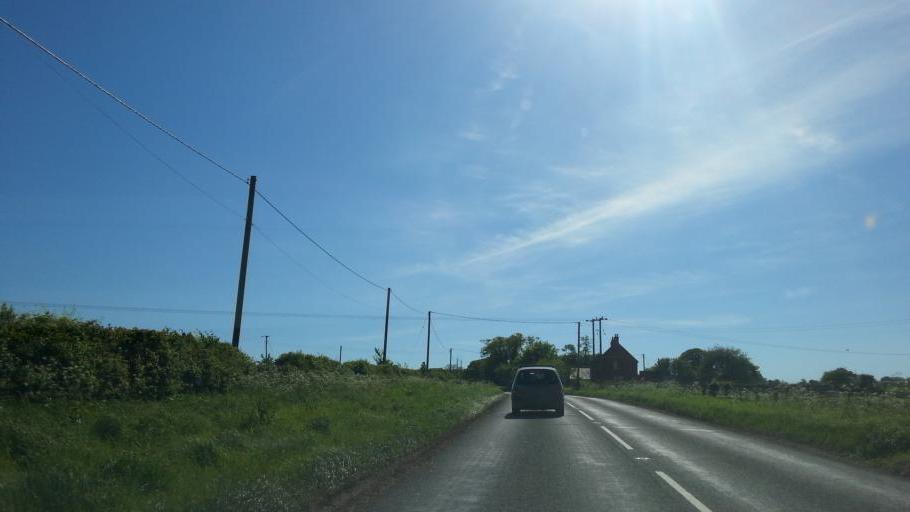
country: GB
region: England
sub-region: Dorset
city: Stalbridge
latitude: 50.9754
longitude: -2.4133
